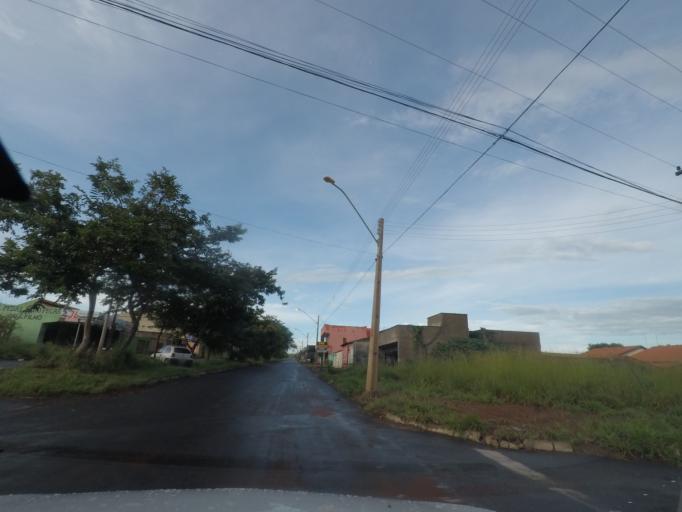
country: BR
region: Goias
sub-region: Goiania
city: Goiania
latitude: -16.7475
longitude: -49.3743
